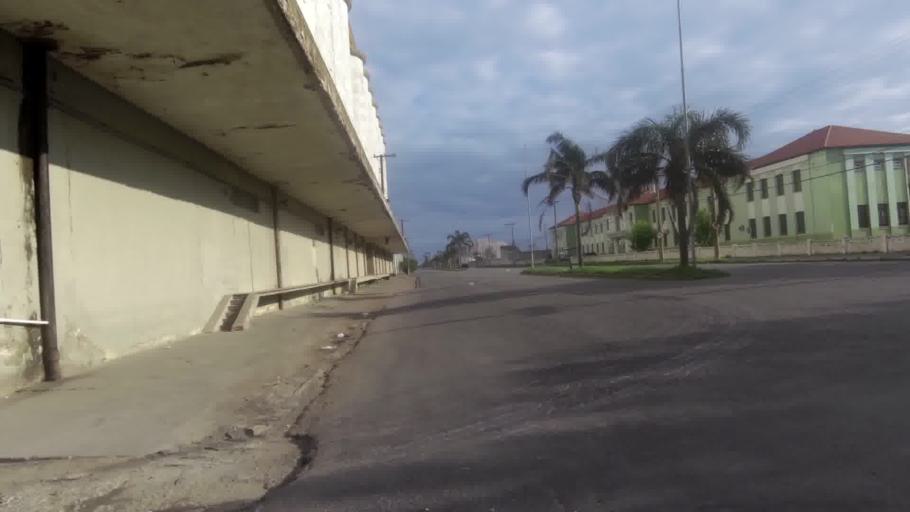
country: BR
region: Rio Grande do Sul
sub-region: Rio Grande
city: Rio Grande
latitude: -32.0346
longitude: -52.0791
